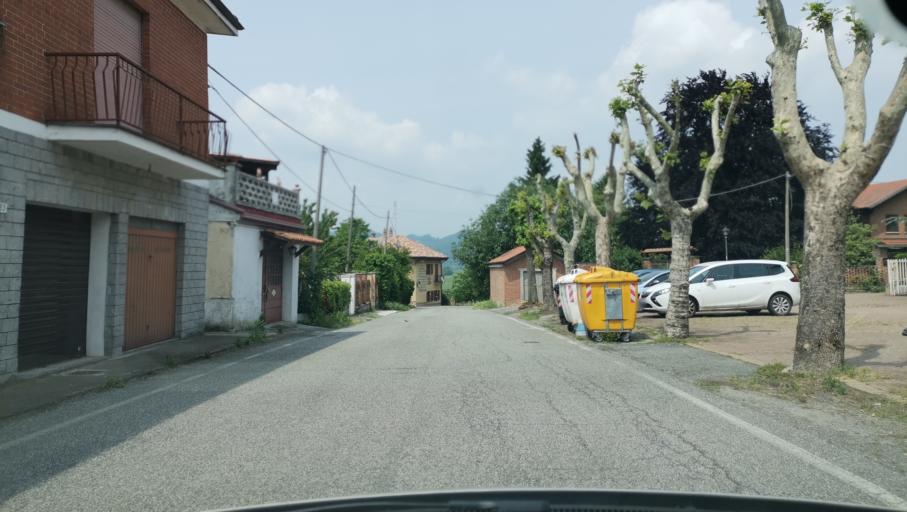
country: IT
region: Piedmont
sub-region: Provincia di Alessandria
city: Castelletto Merli
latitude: 45.0648
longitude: 8.2275
